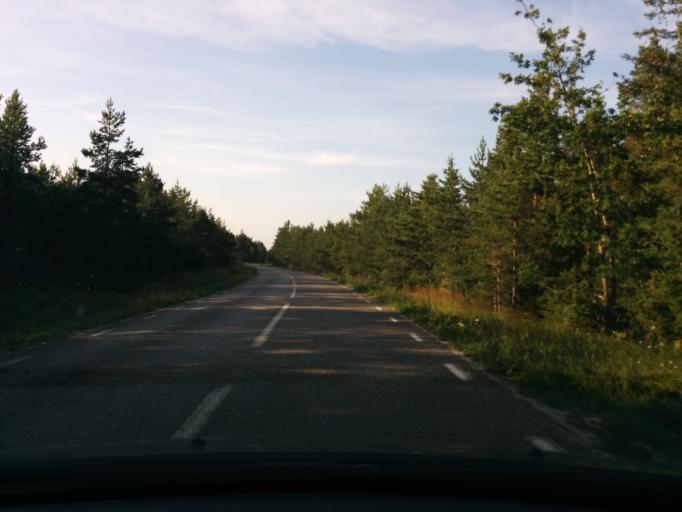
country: SE
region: Gotland
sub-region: Gotland
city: Slite
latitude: 57.5272
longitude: 18.6970
